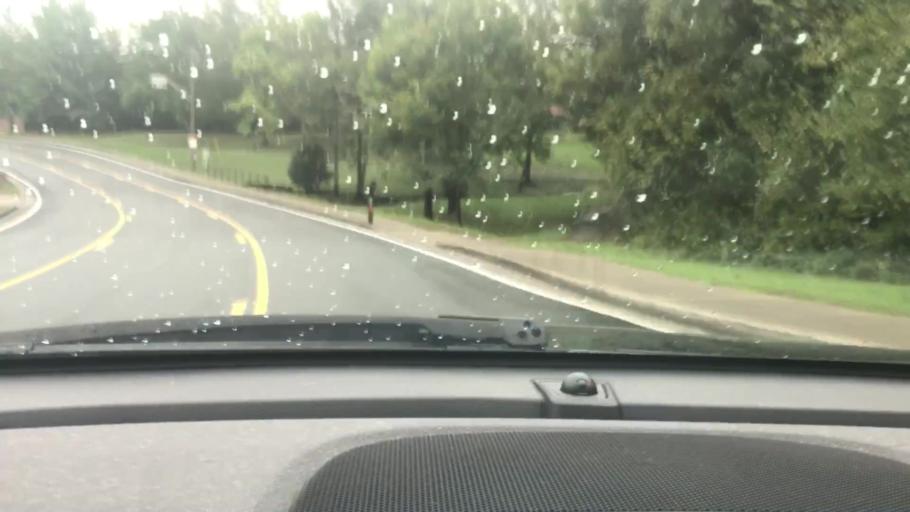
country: US
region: Tennessee
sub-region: Cheatham County
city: Kingston Springs
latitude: 36.0907
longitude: -87.1109
